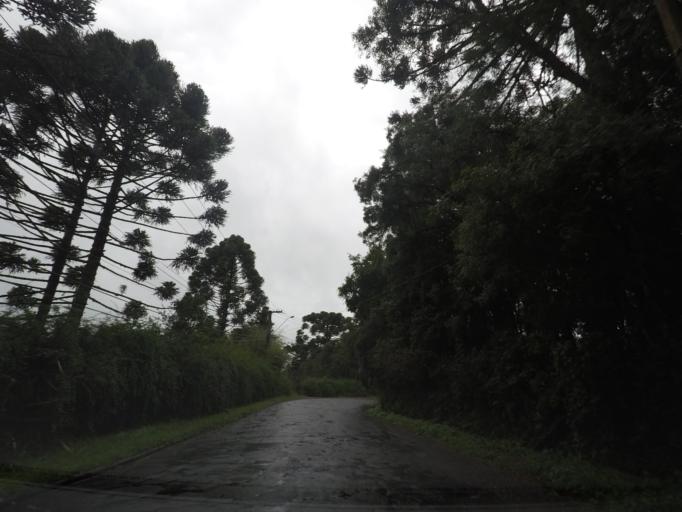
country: BR
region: Parana
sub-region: Campo Largo
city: Campo Largo
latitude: -25.4523
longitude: -49.4485
